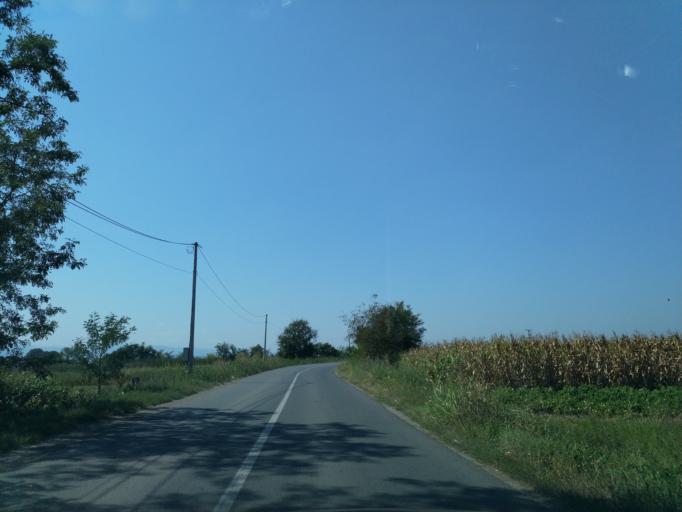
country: RS
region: Central Serbia
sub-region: Rasinski Okrug
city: Krusevac
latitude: 43.6192
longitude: 21.1834
